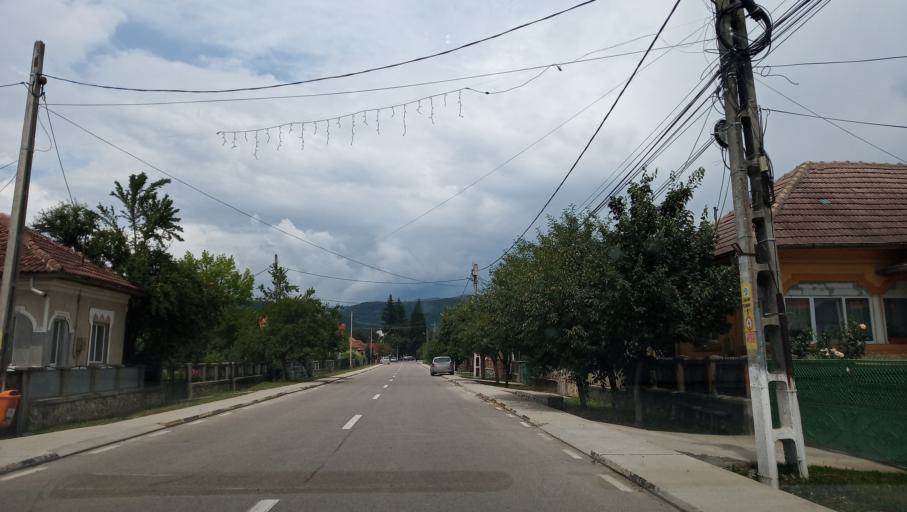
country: RO
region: Gorj
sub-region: Comuna Tismana
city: Tismana
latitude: 45.0516
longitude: 22.9465
